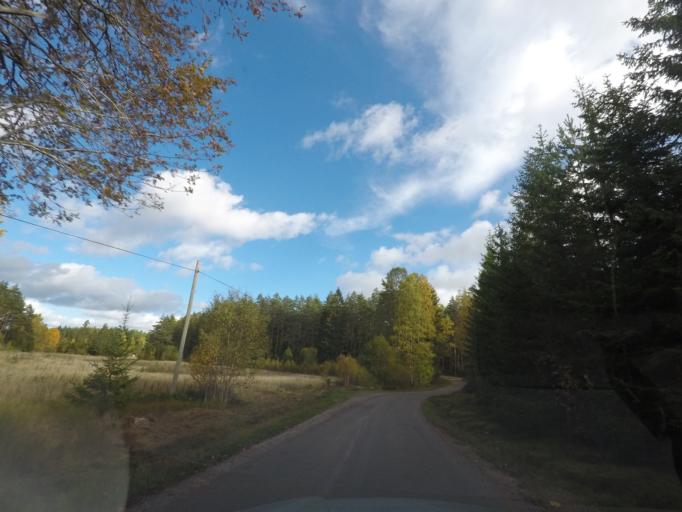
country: SE
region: Vaestmanland
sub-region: Kungsors Kommun
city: Kungsoer
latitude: 59.3322
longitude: 16.1364
